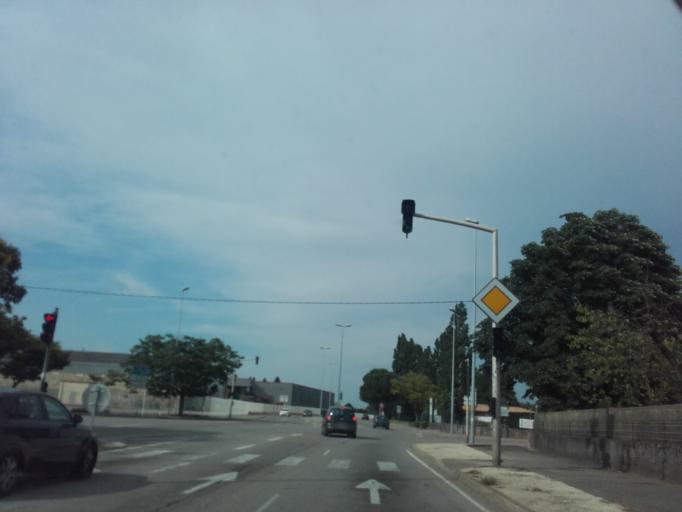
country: FR
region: Rhone-Alpes
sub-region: Departement de la Drome
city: Loriol-sur-Drome
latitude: 44.7530
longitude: 4.8177
